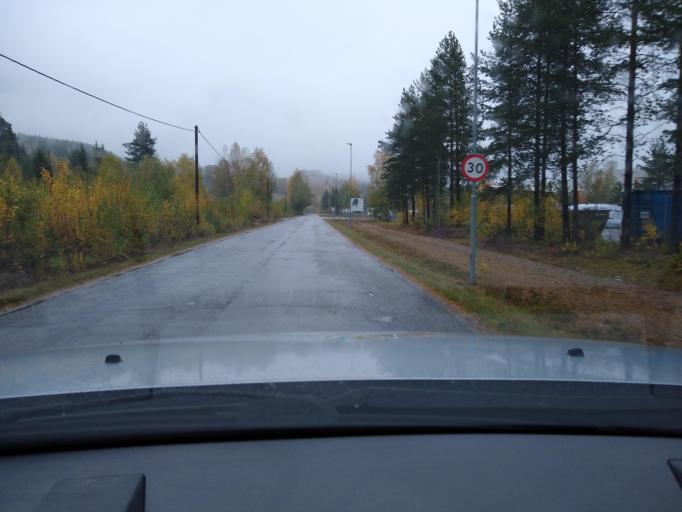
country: NO
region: Oppland
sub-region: Ringebu
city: Ringebu
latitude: 61.5478
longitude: 10.0620
